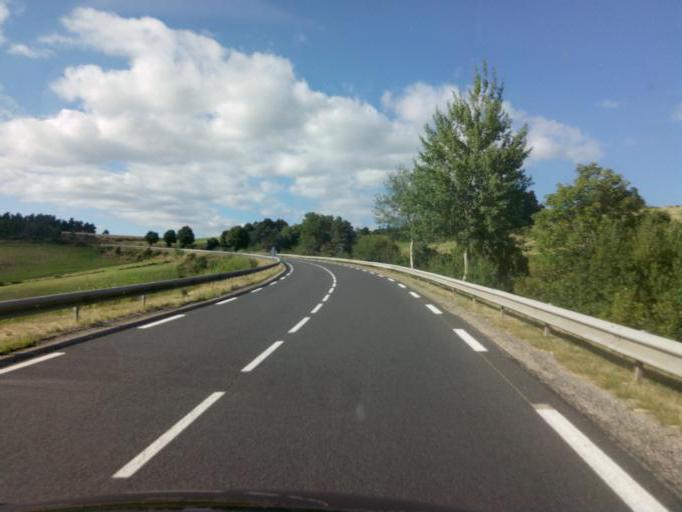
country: FR
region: Auvergne
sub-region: Departement de la Haute-Loire
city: Saint-Paulien
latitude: 45.1658
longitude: 3.8356
